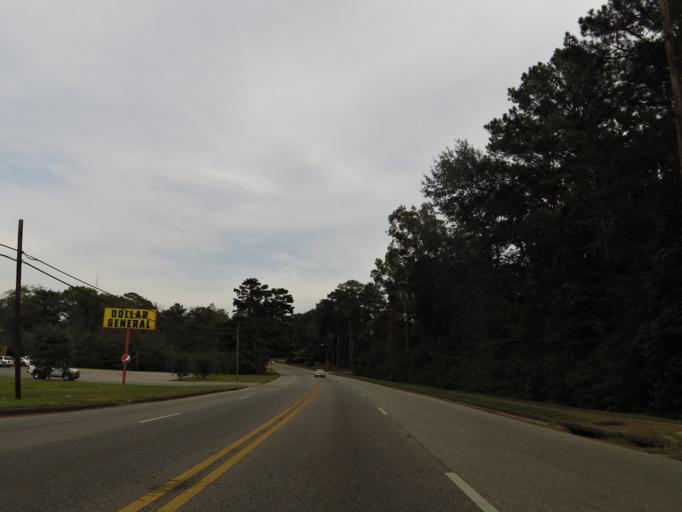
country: US
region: Alabama
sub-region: Monroe County
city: Monroeville
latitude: 31.5262
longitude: -87.3344
